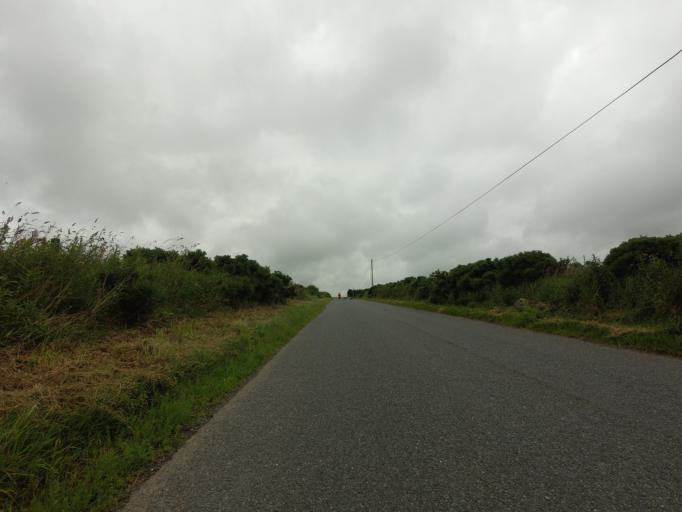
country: GB
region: Scotland
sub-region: Aberdeenshire
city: Turriff
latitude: 57.5438
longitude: -2.2553
